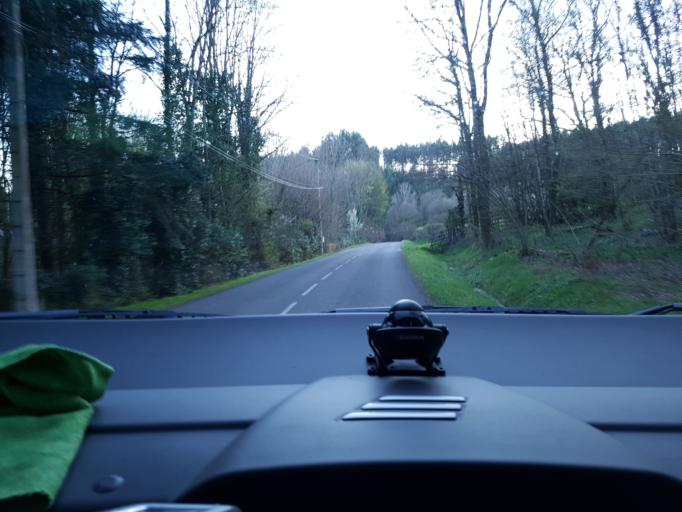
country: FR
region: Bourgogne
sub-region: Departement de Saone-et-Loire
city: Etang-sur-Arroux
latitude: 46.9081
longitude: 4.1327
